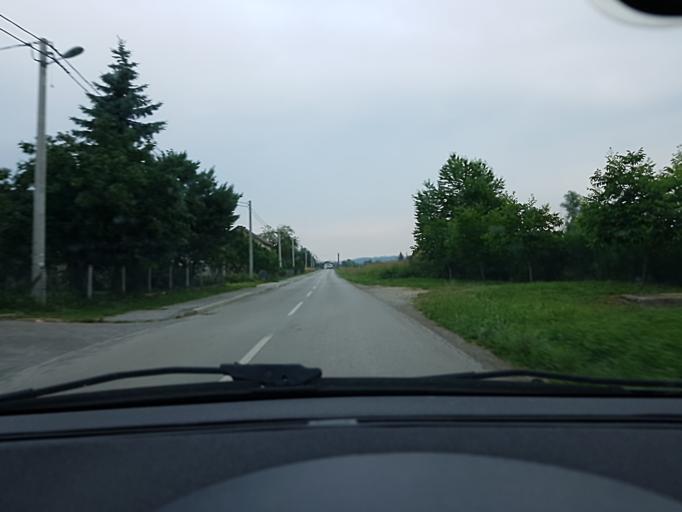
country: HR
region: Zagrebacka
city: Jakovlje
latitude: 45.9863
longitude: 15.8410
